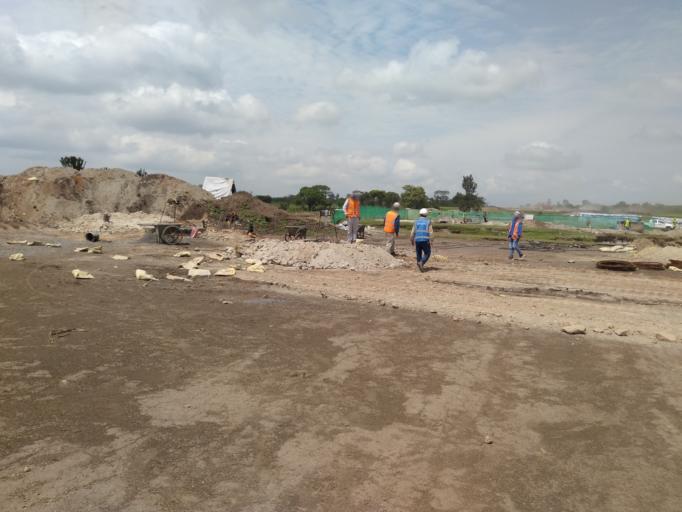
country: ET
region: Oromiya
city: Shashemene
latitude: 7.2705
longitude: 38.5993
